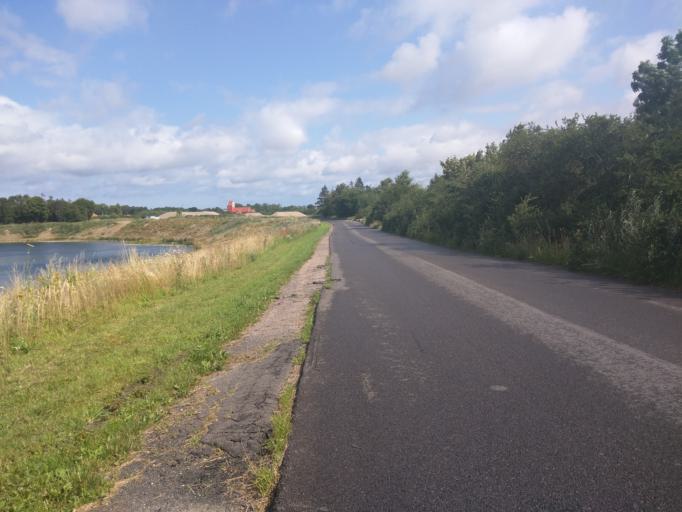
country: DK
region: Zealand
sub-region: Kalundborg Kommune
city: Svebolle
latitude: 55.6770
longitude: 11.3118
